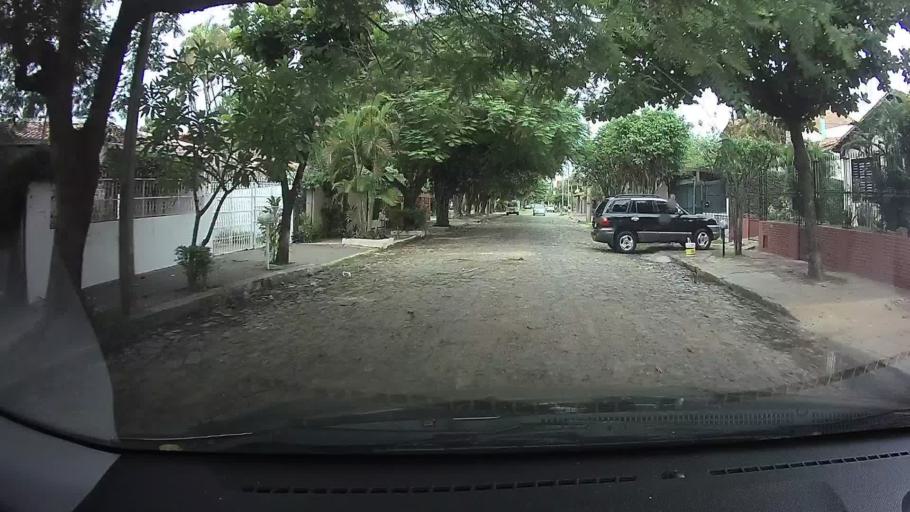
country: PY
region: Asuncion
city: Asuncion
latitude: -25.2727
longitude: -57.5665
